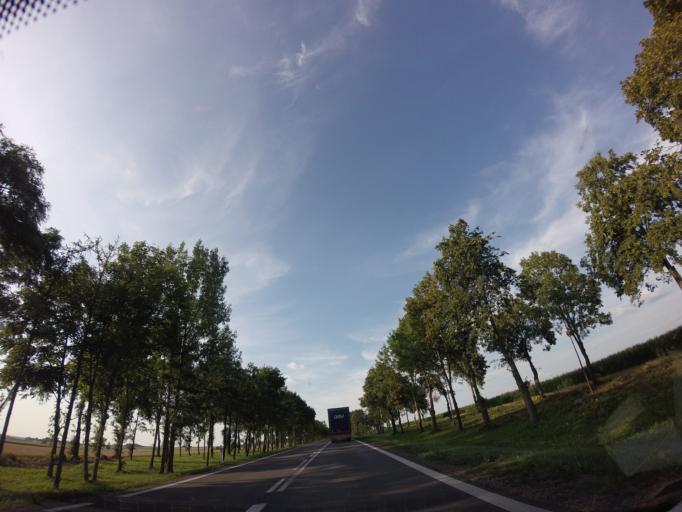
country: PL
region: Podlasie
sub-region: Powiat sokolski
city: Suchowola
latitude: 53.5212
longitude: 23.1059
